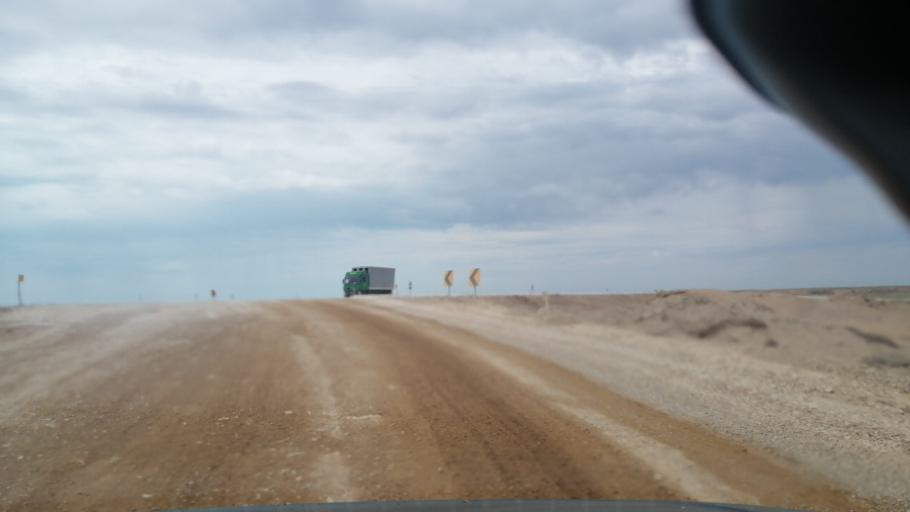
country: KZ
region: Qaraghandy
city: Balqash
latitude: 46.5929
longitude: 74.2712
